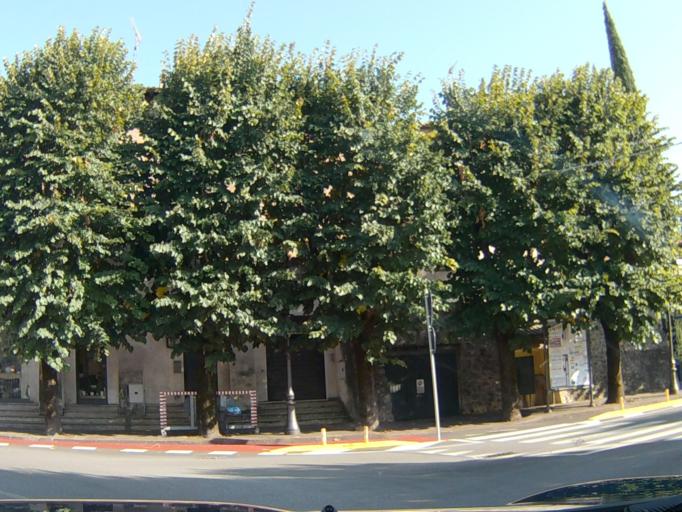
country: IT
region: Lombardy
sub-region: Provincia di Brescia
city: Coccaglio
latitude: 45.5634
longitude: 9.9773
